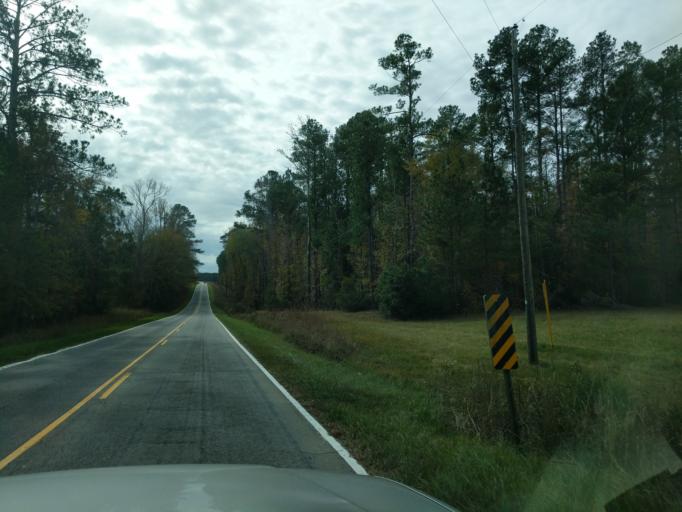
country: US
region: South Carolina
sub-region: Greenwood County
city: Ninety Six
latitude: 34.2099
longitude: -81.8834
